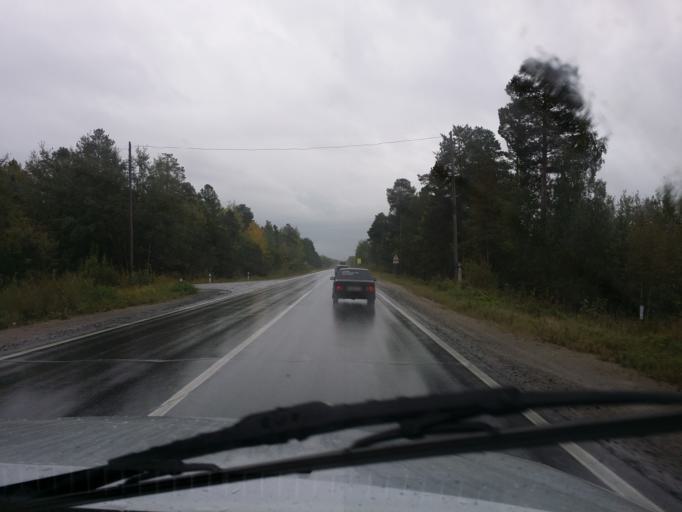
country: RU
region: Khanty-Mansiyskiy Avtonomnyy Okrug
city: Megion
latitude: 61.1547
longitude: 75.7377
